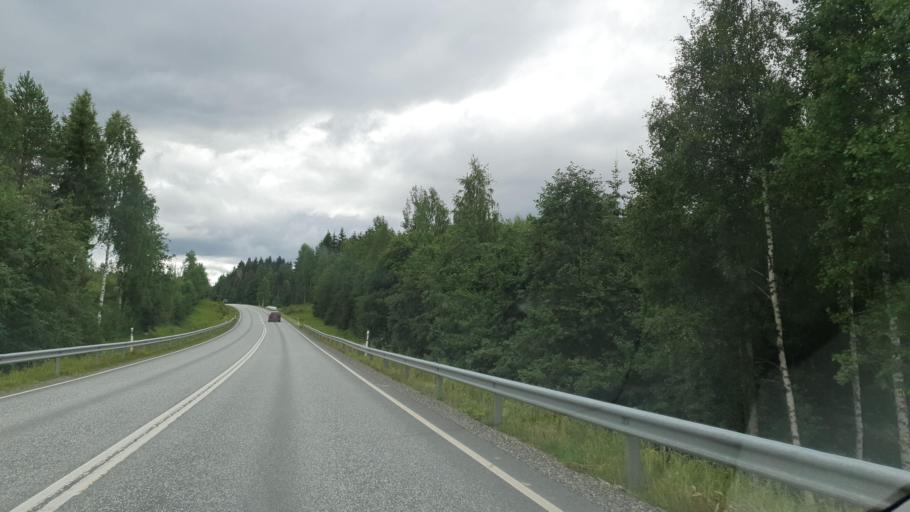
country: FI
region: Northern Savo
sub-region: Ylae-Savo
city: Sonkajaervi
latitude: 63.7568
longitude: 27.3938
